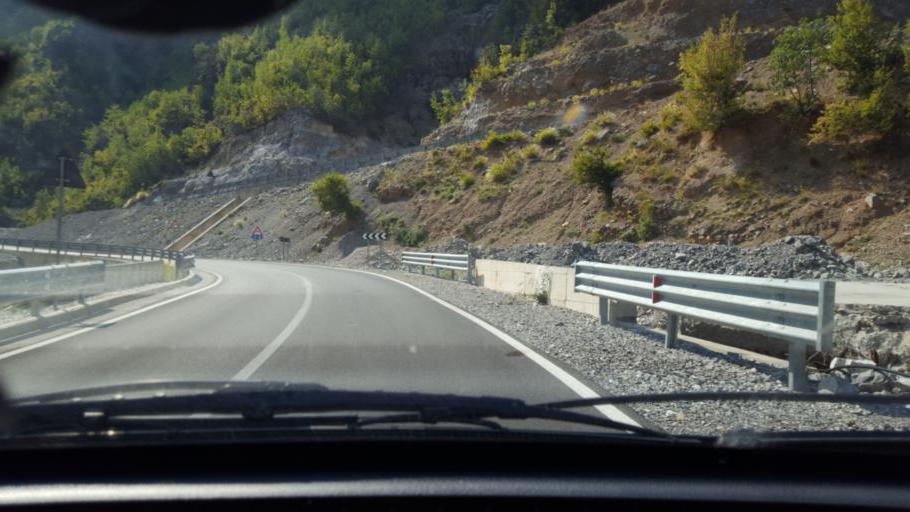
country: AL
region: Shkoder
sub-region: Rrethi i Malesia e Madhe
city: Kastrat
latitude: 42.4134
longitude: 19.5107
